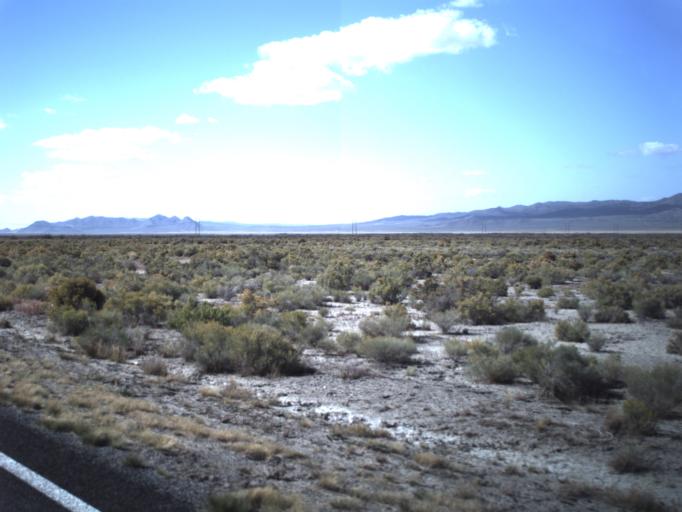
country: US
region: Utah
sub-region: Beaver County
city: Milford
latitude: 38.5836
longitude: -112.9889
